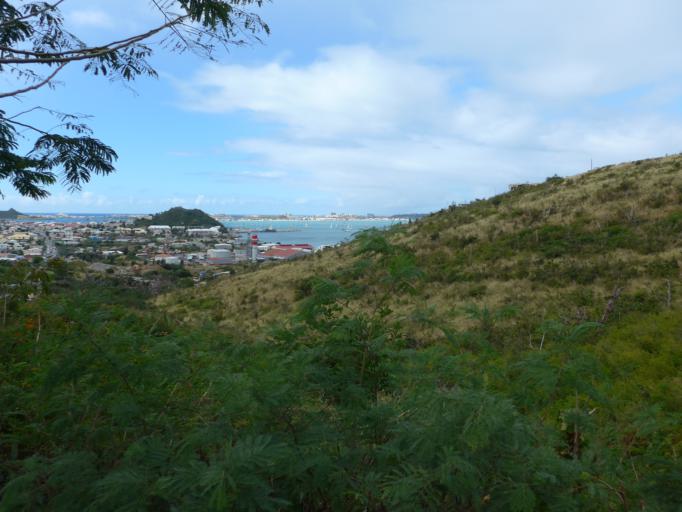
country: MF
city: Marigot
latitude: 18.0800
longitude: -63.0757
